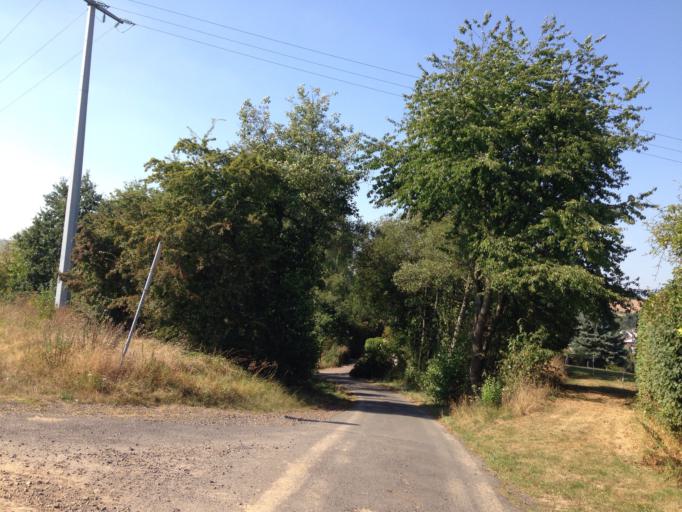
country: DE
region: Hesse
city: Staufenberg
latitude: 50.6559
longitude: 8.7490
